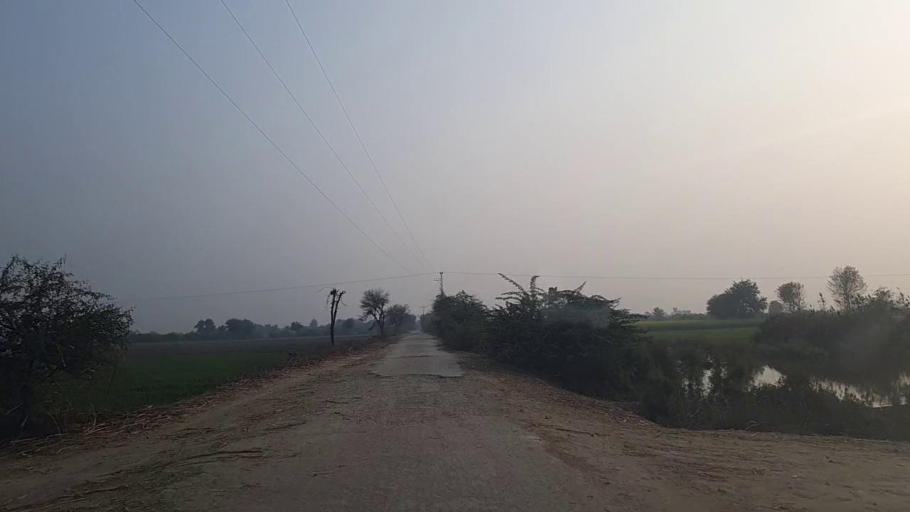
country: PK
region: Sindh
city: Sinjhoro
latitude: 26.1099
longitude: 68.7965
